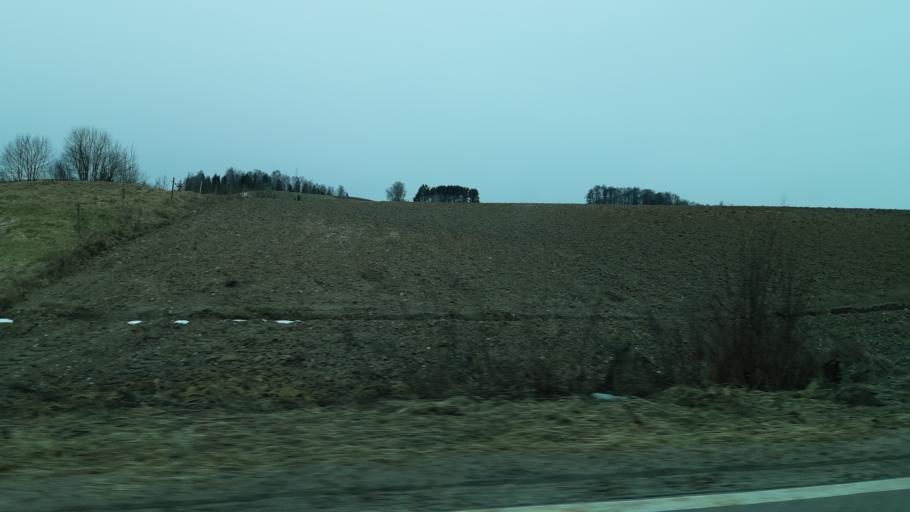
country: PL
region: Podlasie
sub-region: Suwalki
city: Suwalki
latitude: 54.3309
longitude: 22.9502
